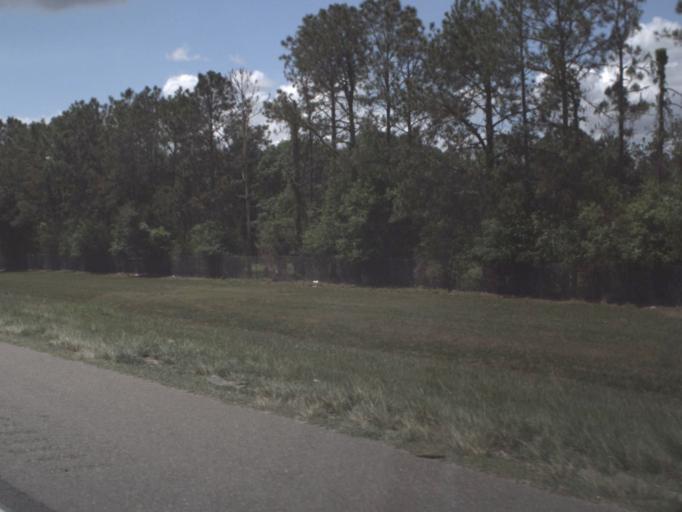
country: US
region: Florida
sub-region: Orange County
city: Ocoee
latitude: 28.5891
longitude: -81.5577
